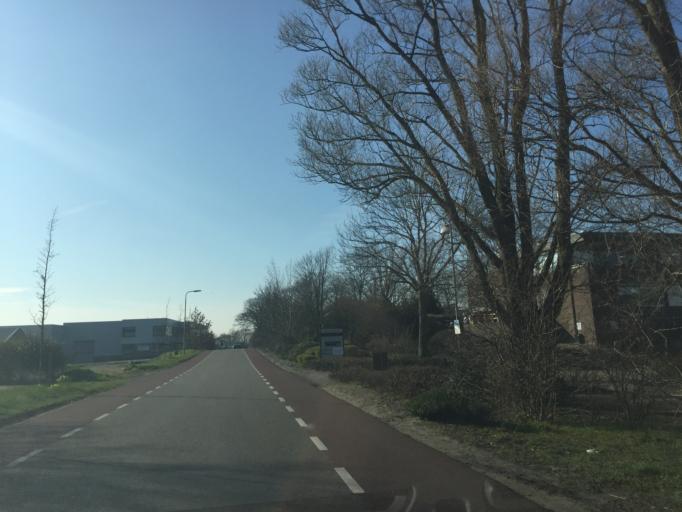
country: NL
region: South Holland
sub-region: Gemeente Hillegom
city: Hillegom
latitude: 52.3033
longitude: 4.5788
